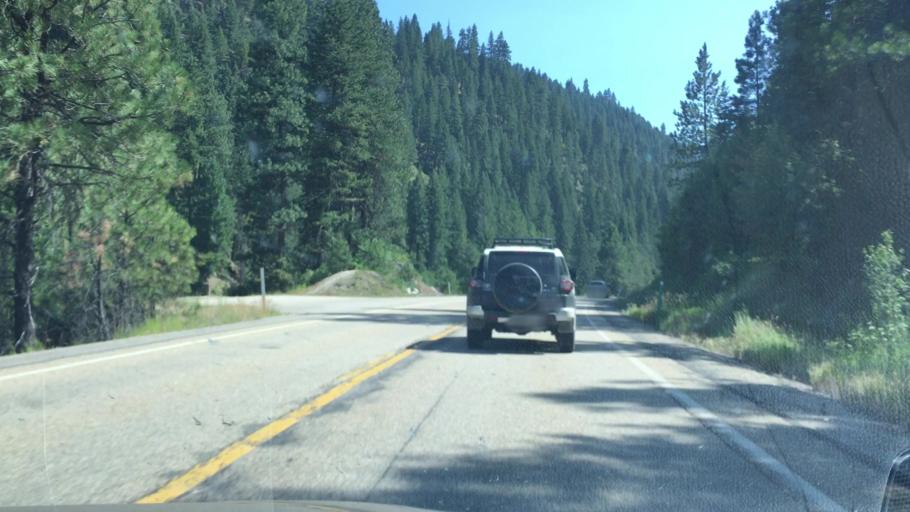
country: US
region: Idaho
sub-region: Valley County
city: Cascade
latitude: 44.2124
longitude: -116.1070
